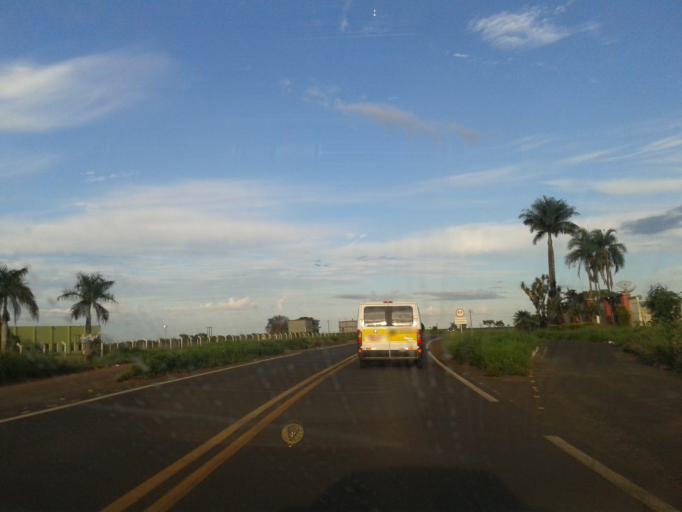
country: BR
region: Minas Gerais
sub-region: Araguari
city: Araguari
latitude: -18.6406
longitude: -48.2221
